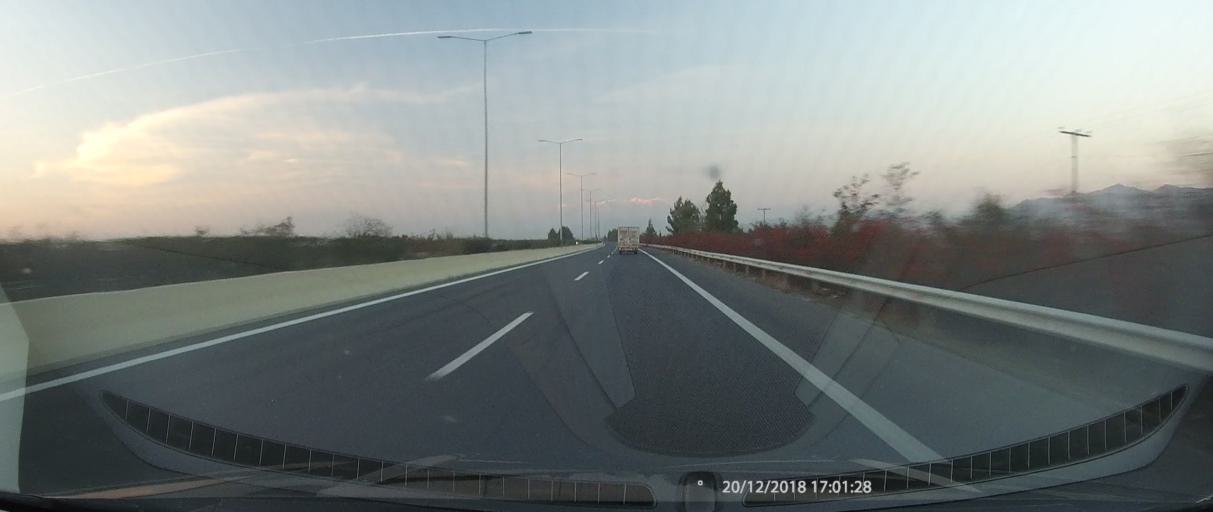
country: GR
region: Thessaly
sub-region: Nomos Larisis
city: Platykampos
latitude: 39.6560
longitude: 22.5067
